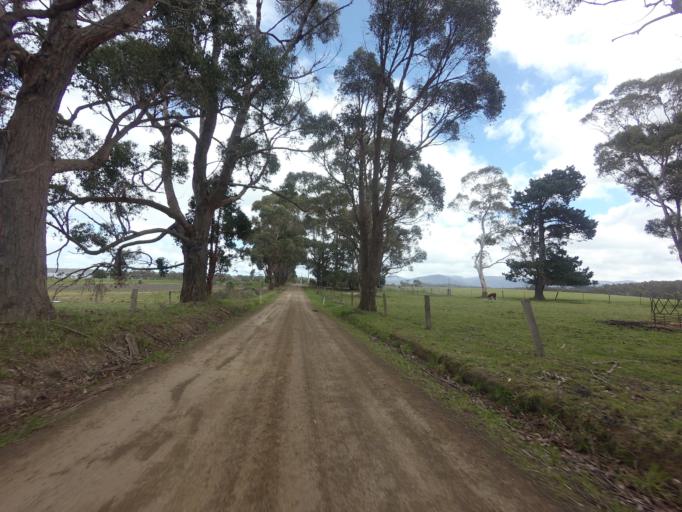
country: AU
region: Tasmania
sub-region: Huon Valley
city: Geeveston
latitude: -43.4290
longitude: 146.9928
